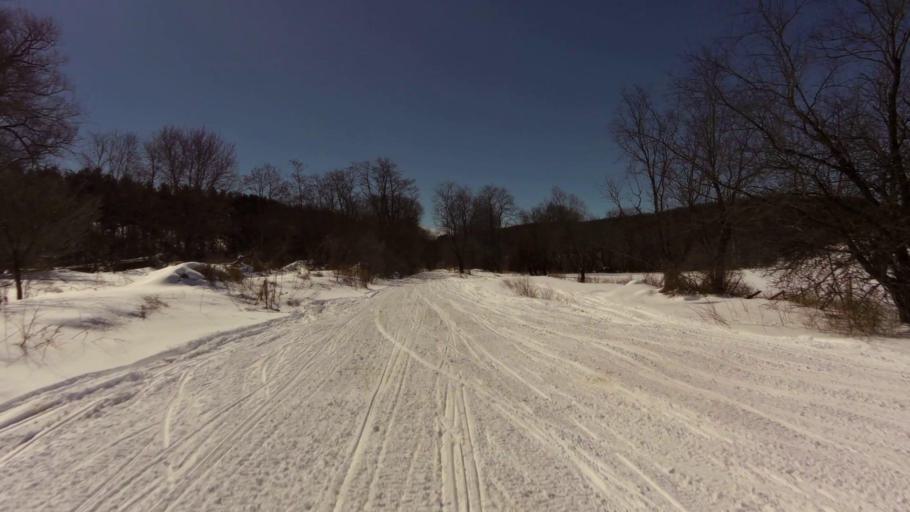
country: US
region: New York
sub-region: Cattaraugus County
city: Delevan
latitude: 42.4304
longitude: -78.4490
